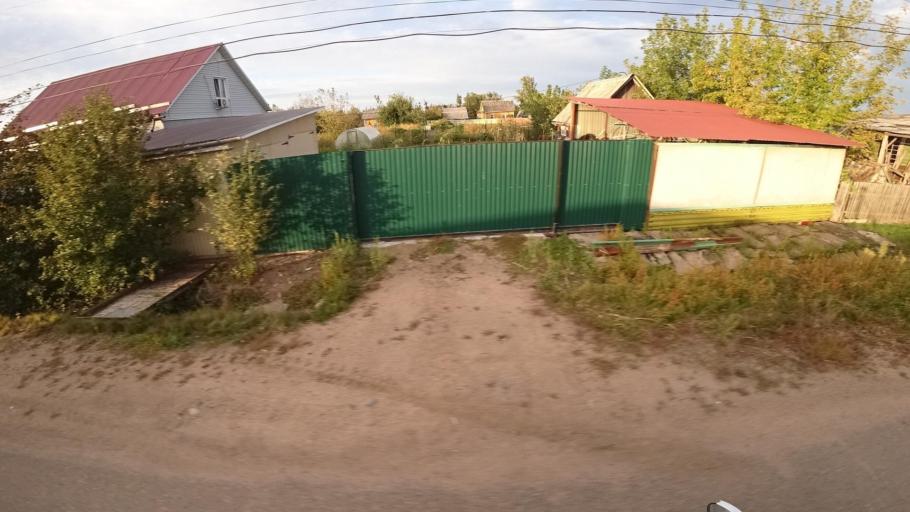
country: RU
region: Primorskiy
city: Yakovlevka
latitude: 44.4247
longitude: 133.4856
